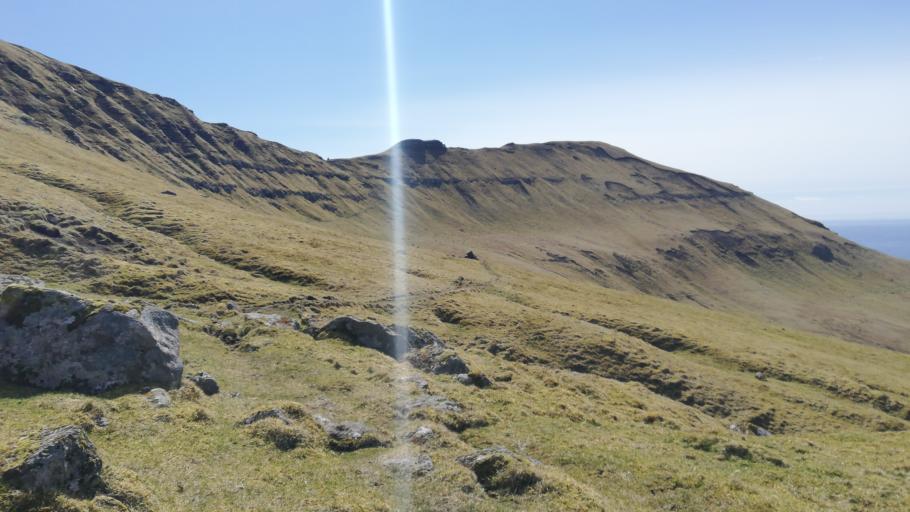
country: FO
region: Streymoy
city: Kollafjordhur
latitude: 62.0650
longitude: -6.9806
